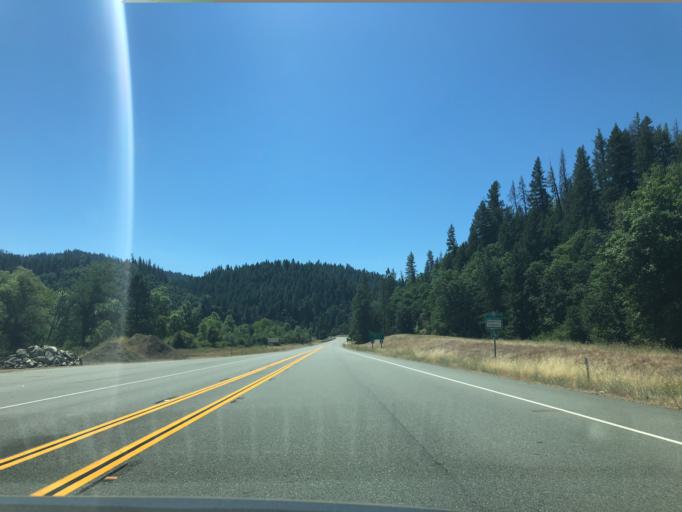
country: US
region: California
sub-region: Trinity County
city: Weaverville
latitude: 40.6581
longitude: -122.9430
